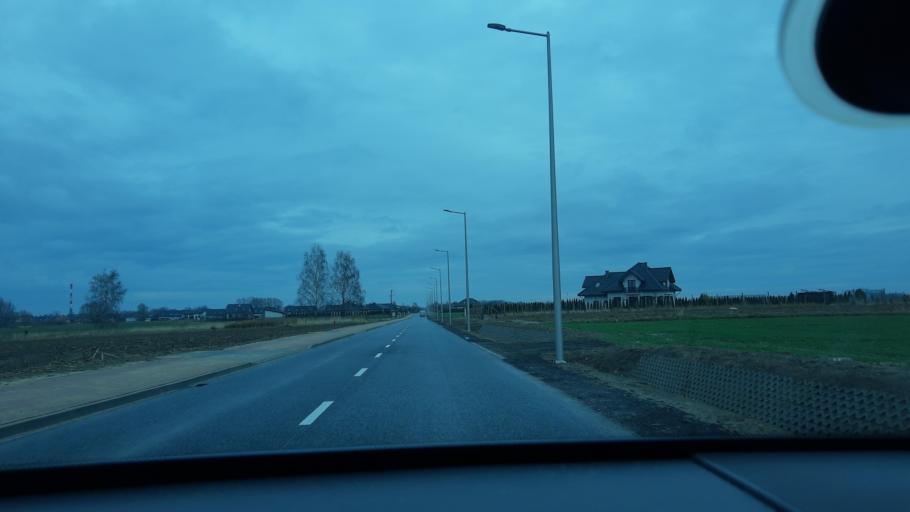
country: PL
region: Lodz Voivodeship
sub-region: Powiat sieradzki
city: Sieradz
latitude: 51.5832
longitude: 18.6790
